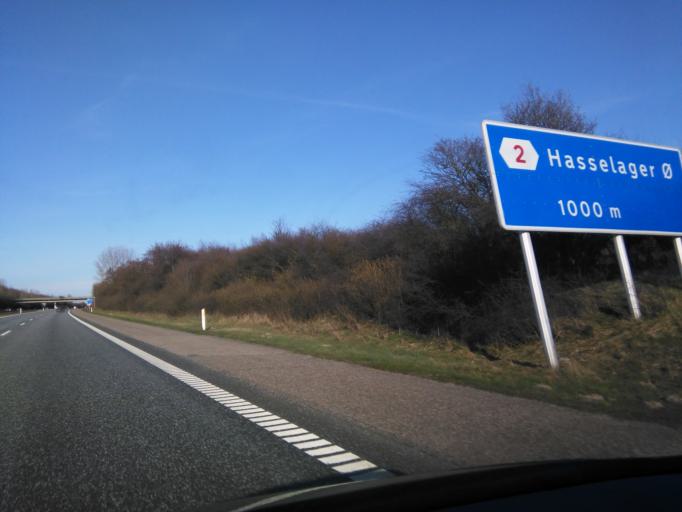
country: DK
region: Central Jutland
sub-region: Arhus Kommune
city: Kolt
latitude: 56.1142
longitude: 10.0638
